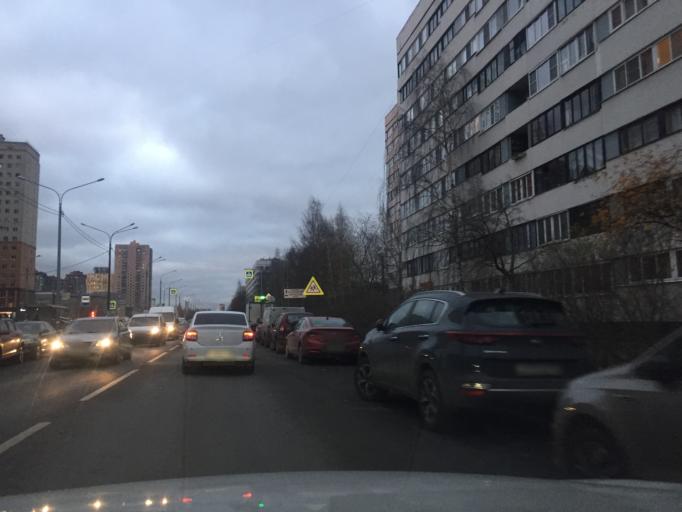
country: RU
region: St.-Petersburg
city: Grazhdanka
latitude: 60.0307
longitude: 30.4061
